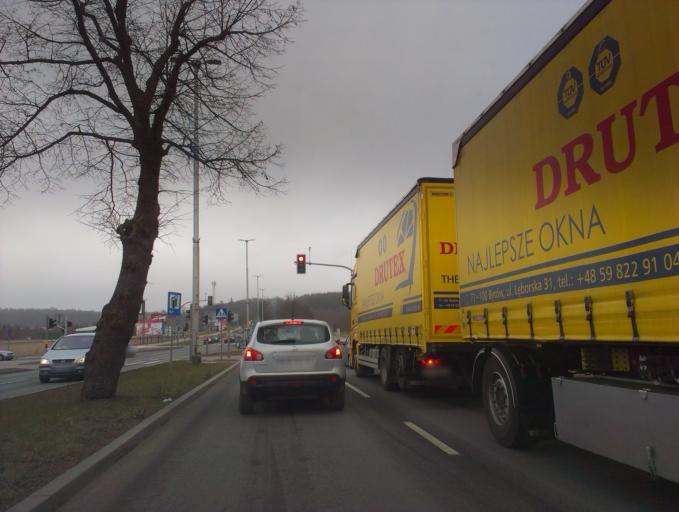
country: PL
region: West Pomeranian Voivodeship
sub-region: Koszalin
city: Koszalin
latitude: 54.2047
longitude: 16.2043
